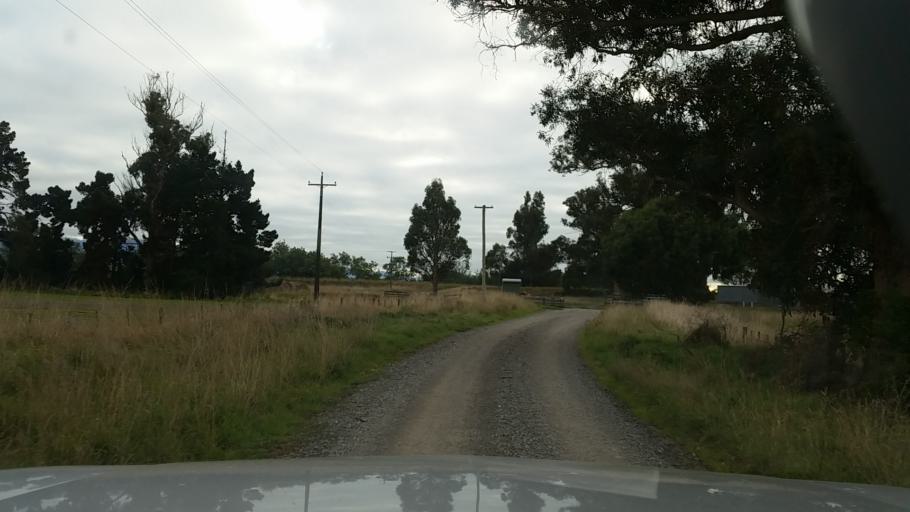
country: NZ
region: Marlborough
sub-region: Marlborough District
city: Blenheim
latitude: -41.5010
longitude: 174.0335
